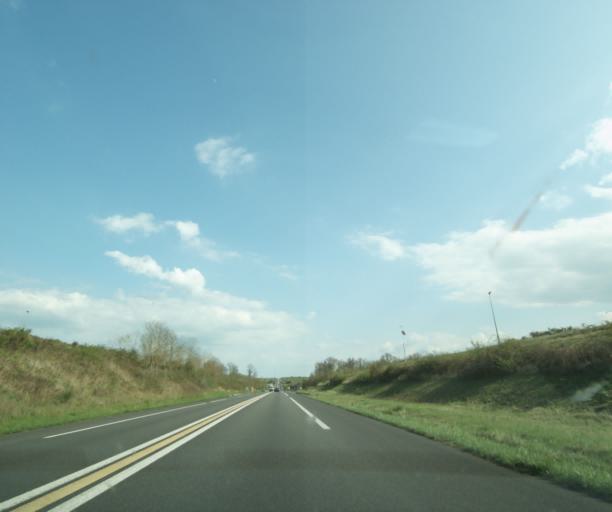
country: FR
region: Auvergne
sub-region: Departement de l'Allier
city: Diou
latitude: 46.5039
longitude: 3.7810
